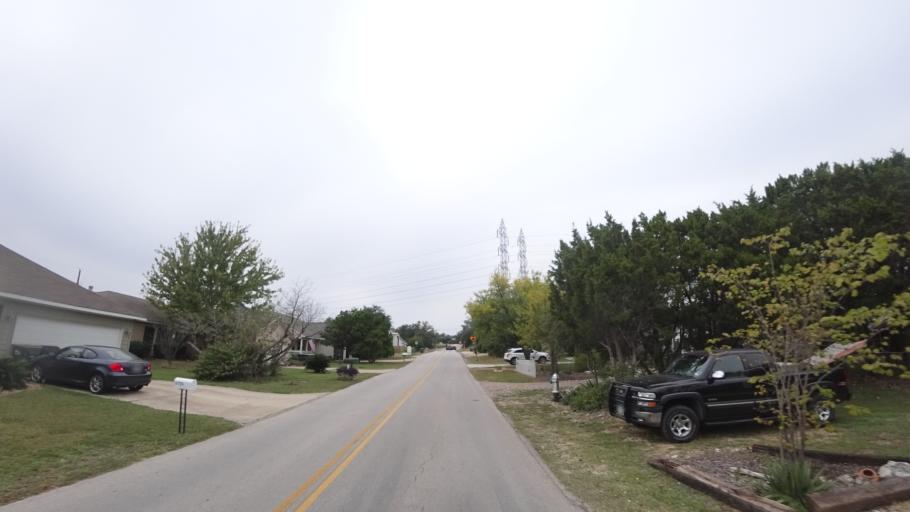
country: US
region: Texas
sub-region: Travis County
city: Hudson Bend
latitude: 30.3855
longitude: -97.9251
